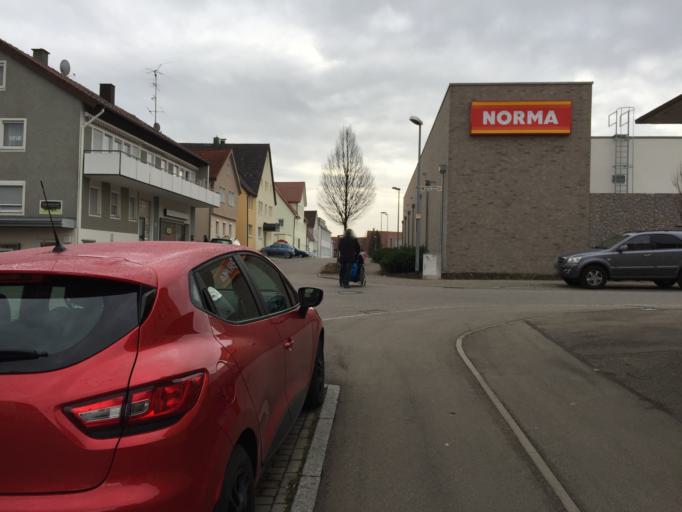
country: DE
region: Baden-Wuerttemberg
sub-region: Freiburg Region
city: Trossingen
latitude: 48.0735
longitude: 8.6346
